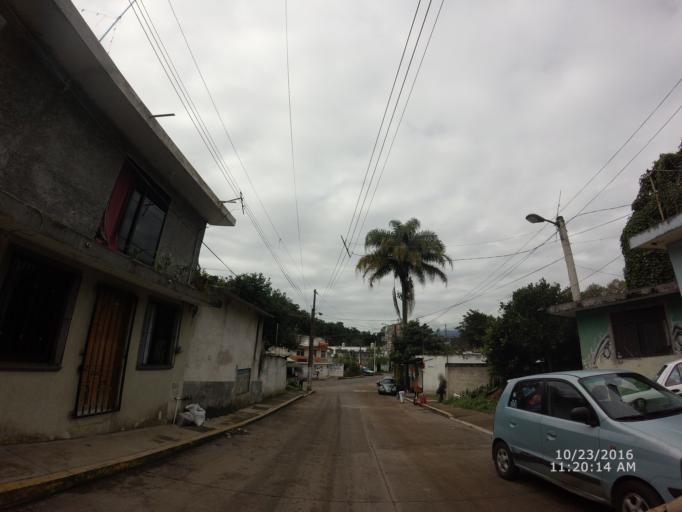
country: MX
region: Veracruz
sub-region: Tlalnelhuayocan
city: Guadalupe Victoria
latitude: 19.5516
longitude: -96.9535
